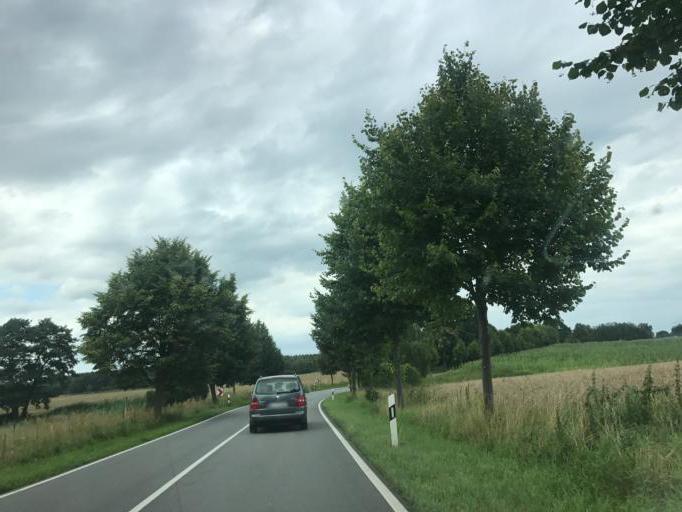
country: DE
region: Mecklenburg-Vorpommern
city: Rechlin
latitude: 53.2640
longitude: 12.7878
